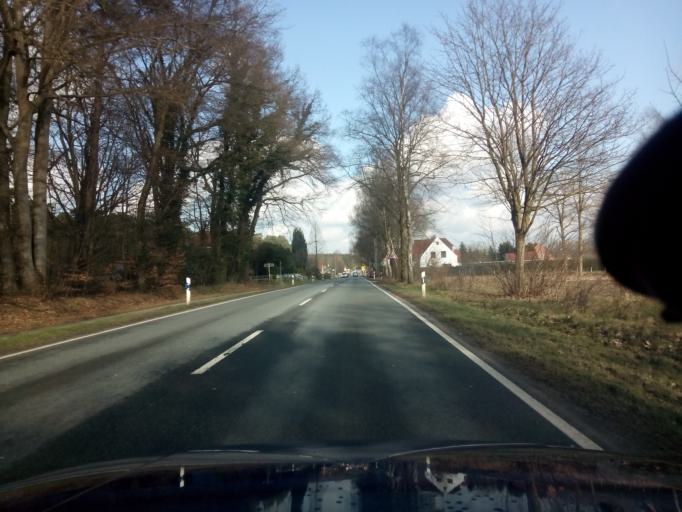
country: DE
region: Lower Saxony
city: Hambergen
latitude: 53.2820
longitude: 8.8237
